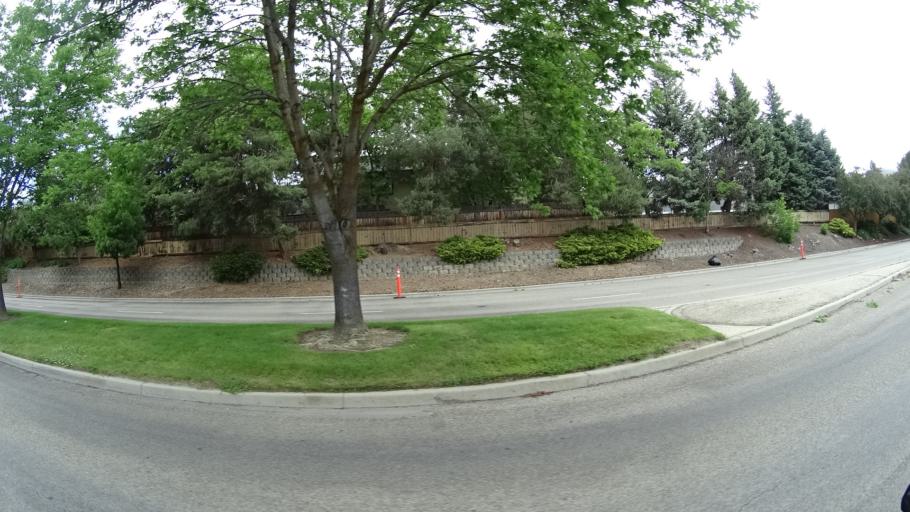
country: US
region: Idaho
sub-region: Ada County
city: Boise
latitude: 43.5825
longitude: -116.1698
